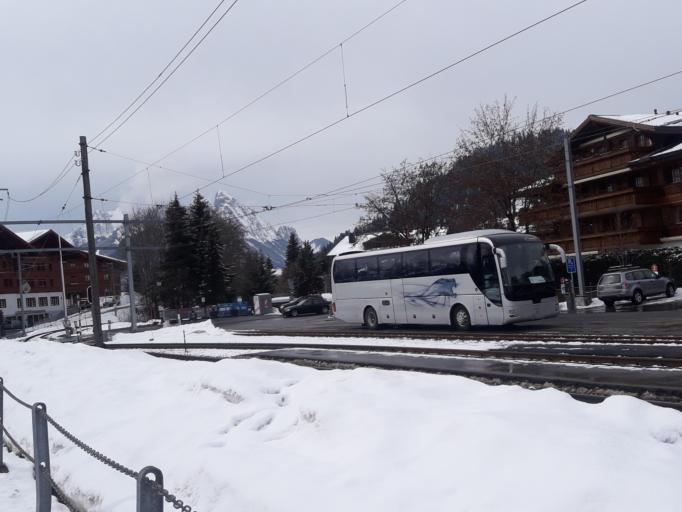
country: CH
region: Bern
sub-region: Obersimmental-Saanen District
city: Gstaad
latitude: 46.5042
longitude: 7.2911
